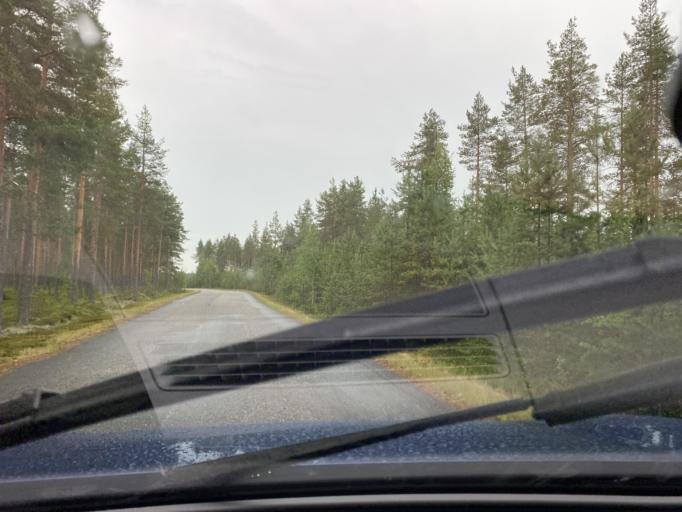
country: FI
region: Central Ostrobothnia
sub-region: Kaustinen
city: Halsua
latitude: 63.4100
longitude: 23.9742
